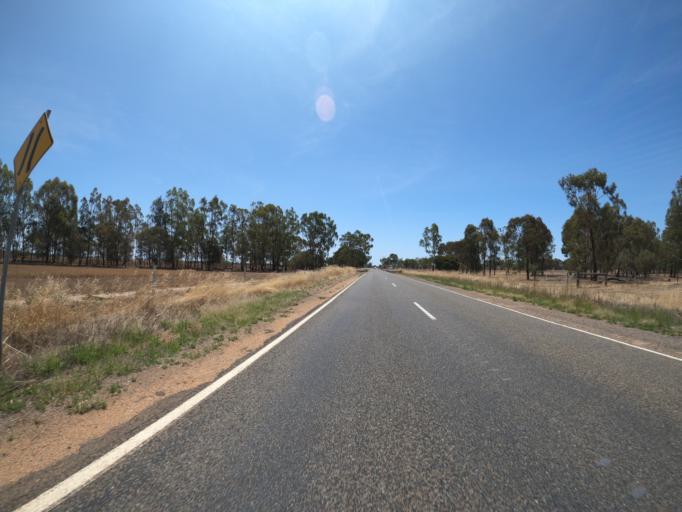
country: AU
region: Victoria
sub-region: Moira
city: Yarrawonga
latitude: -36.1610
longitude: 145.9672
